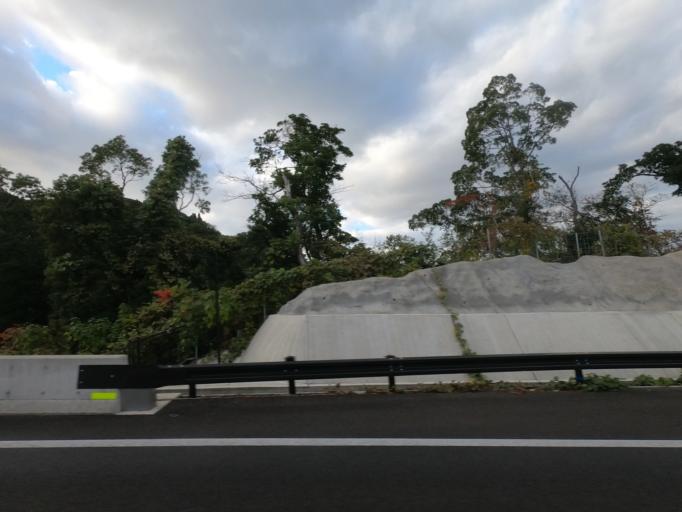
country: JP
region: Kumamoto
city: Minamata
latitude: 32.2251
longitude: 130.4336
